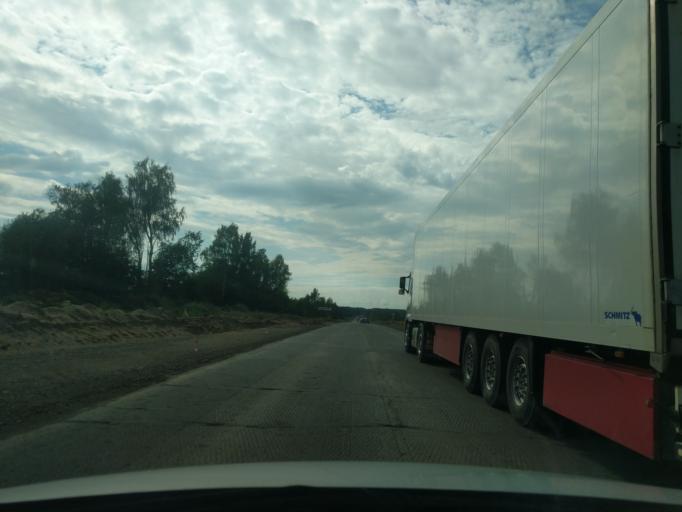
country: RU
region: Kostroma
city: Sudislavl'
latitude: 57.8602
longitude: 41.6149
